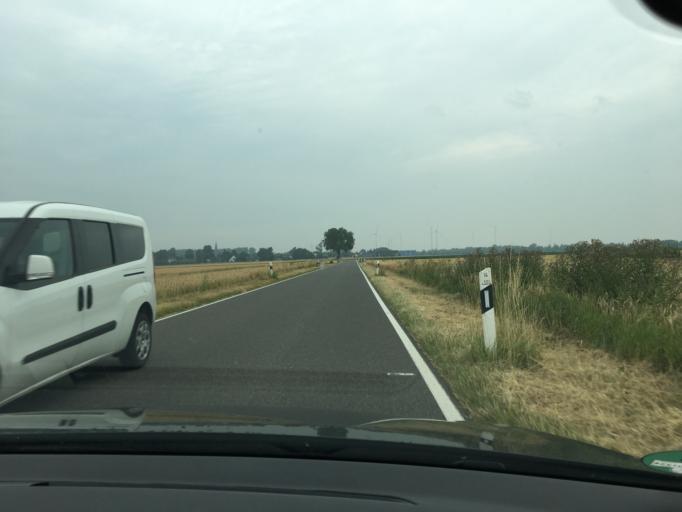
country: DE
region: North Rhine-Westphalia
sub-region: Regierungsbezirk Koln
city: Titz
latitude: 51.0733
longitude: 6.4116
